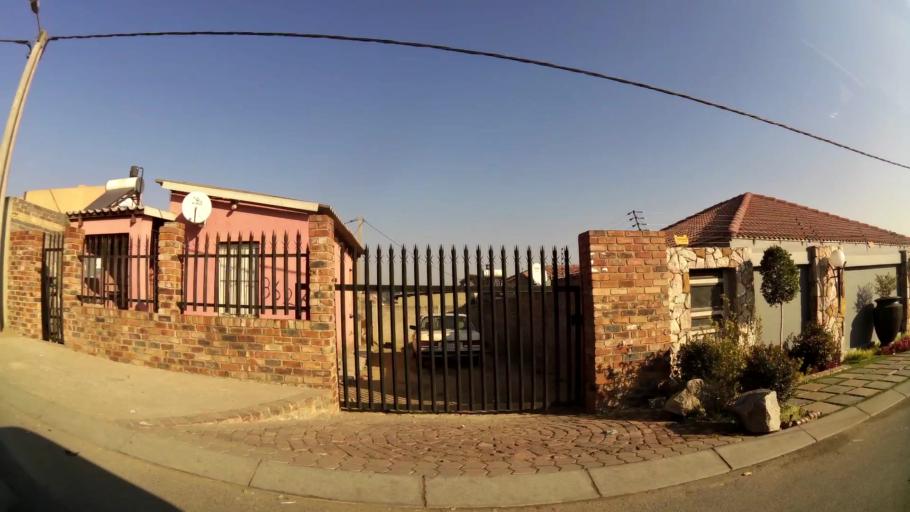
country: ZA
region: Gauteng
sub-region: City of Johannesburg Metropolitan Municipality
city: Modderfontein
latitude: -26.0909
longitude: 28.1121
